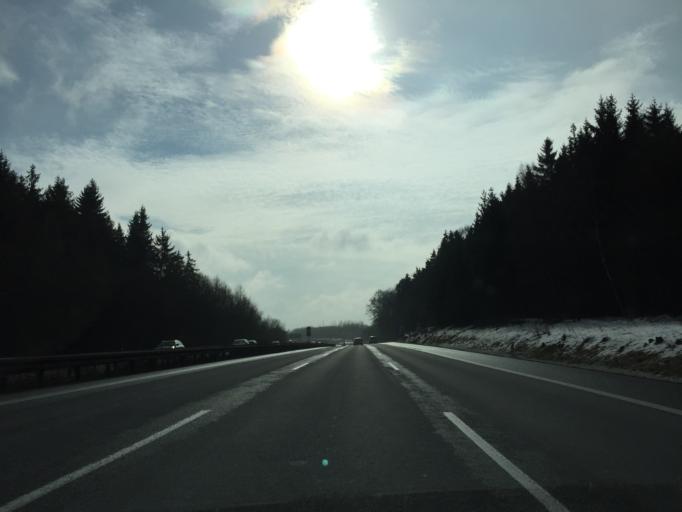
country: DE
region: Bavaria
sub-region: Upper Bavaria
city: Denkendorf
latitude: 48.9565
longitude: 11.4268
